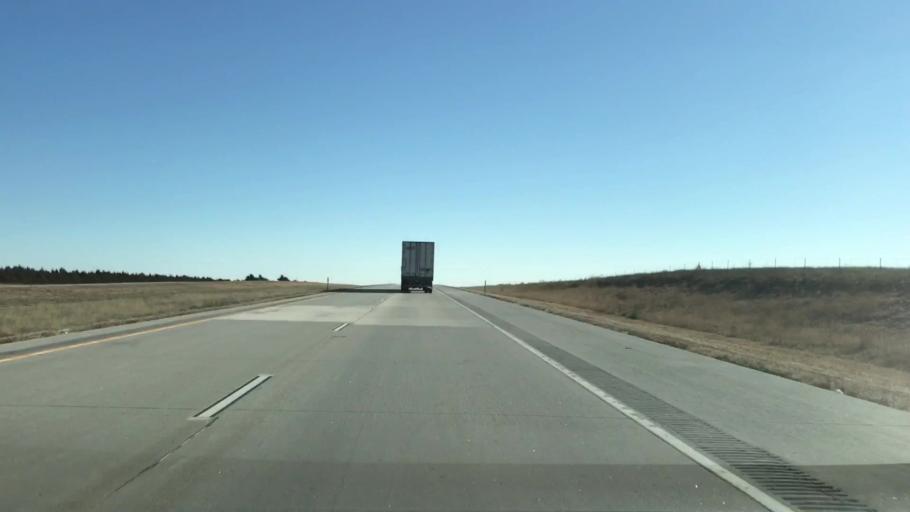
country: US
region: Colorado
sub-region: Kit Carson County
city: Burlington
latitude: 39.2940
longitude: -102.7983
